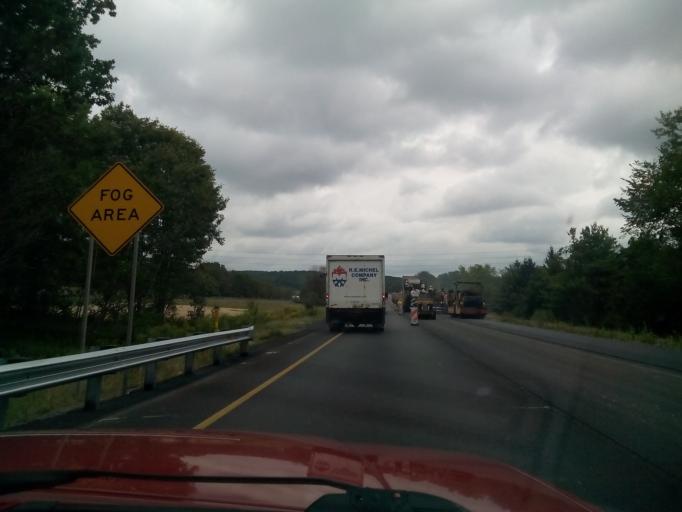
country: US
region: Pennsylvania
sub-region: Jefferson County
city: Falls Creek
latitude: 41.1500
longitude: -78.8630
